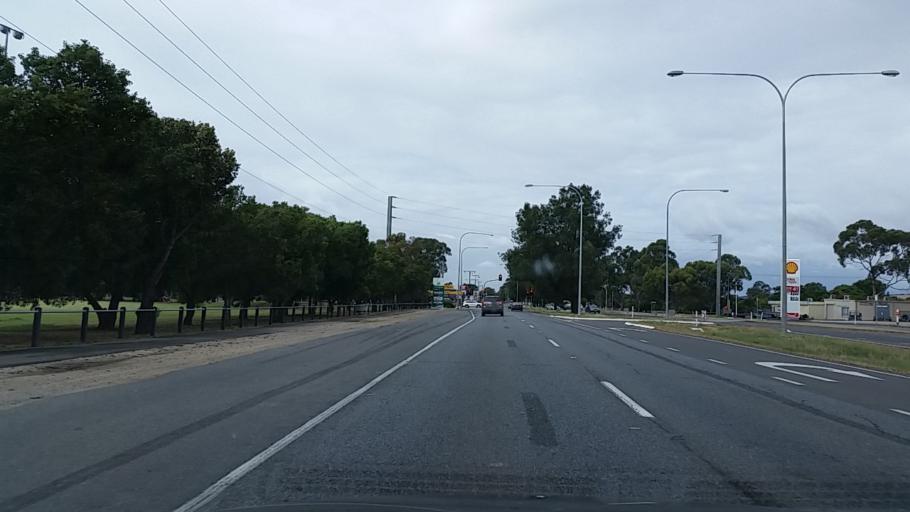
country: AU
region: South Australia
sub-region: Playford
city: Smithfield
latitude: -34.6852
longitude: 138.6922
